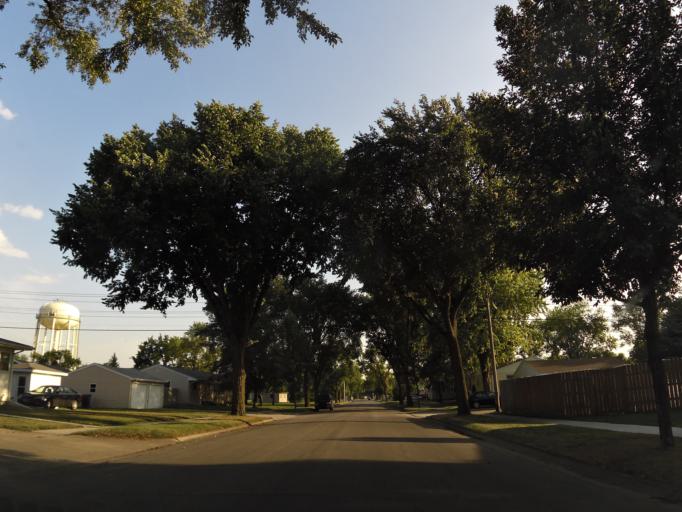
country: US
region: North Dakota
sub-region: Grand Forks County
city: Grand Forks
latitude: 47.8996
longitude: -97.0405
